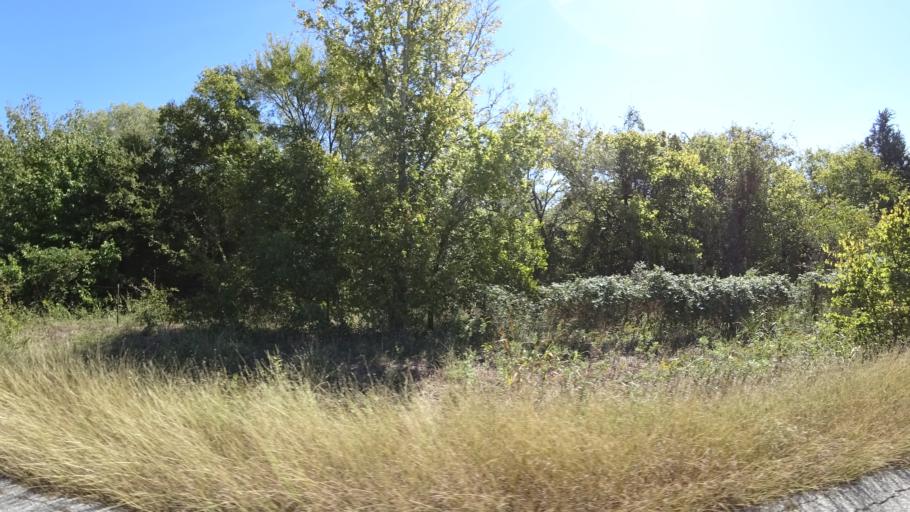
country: US
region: Texas
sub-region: Travis County
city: Austin
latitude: 30.2009
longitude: -97.6884
